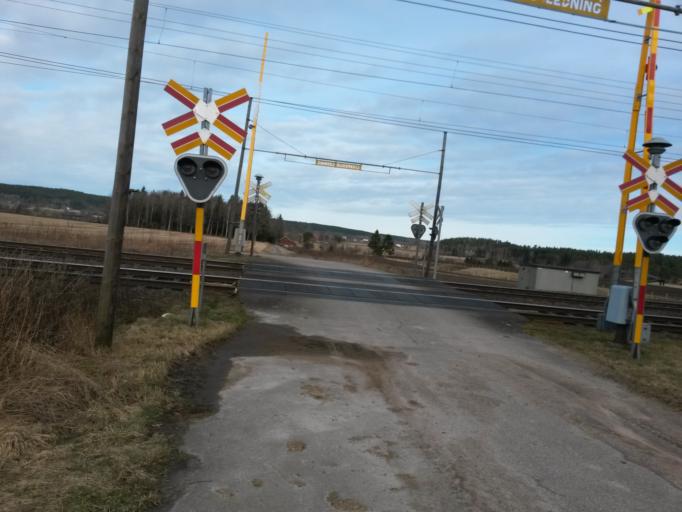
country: SE
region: Vaestra Goetaland
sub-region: Vargarda Kommun
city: Jonstorp
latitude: 57.9847
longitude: 12.6392
